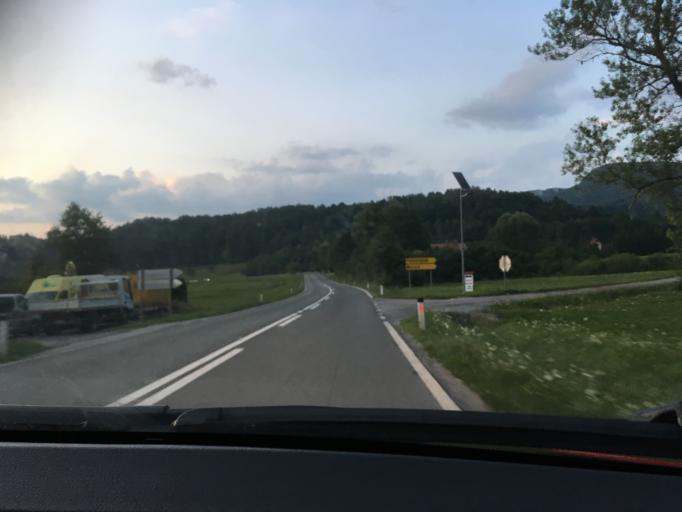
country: SI
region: Pivka
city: Pivka
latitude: 45.5958
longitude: 14.2040
